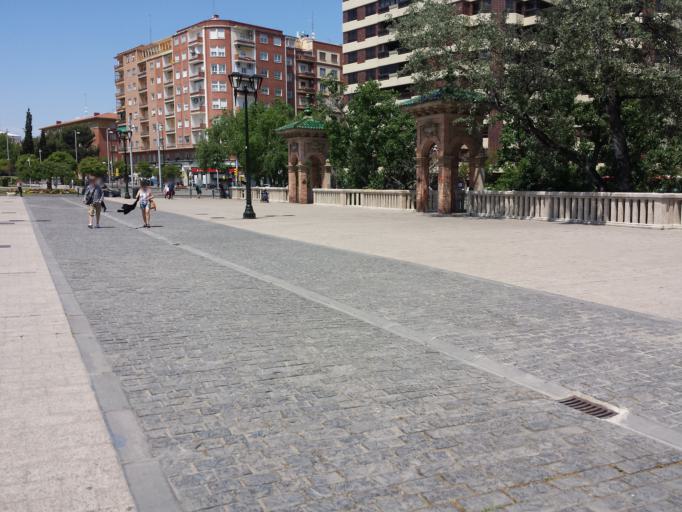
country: ES
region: Aragon
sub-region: Provincia de Zaragoza
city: Delicias
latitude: 41.6369
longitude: -0.8973
